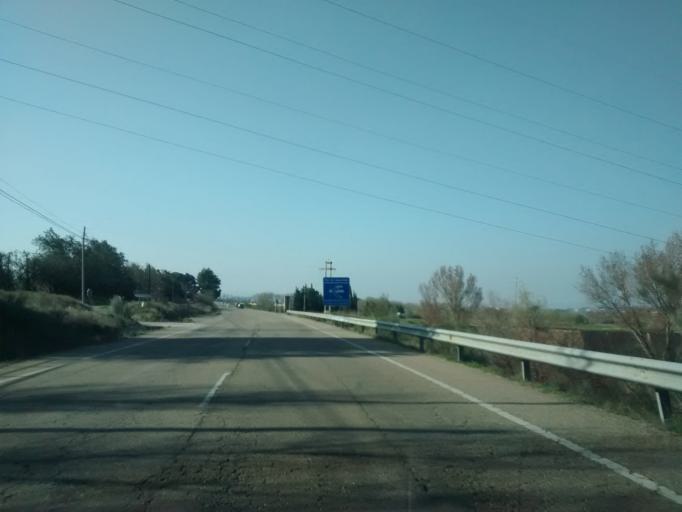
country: ES
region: Aragon
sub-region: Provincia de Zaragoza
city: Villanueva de Gallego
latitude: 41.7429
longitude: -0.8059
